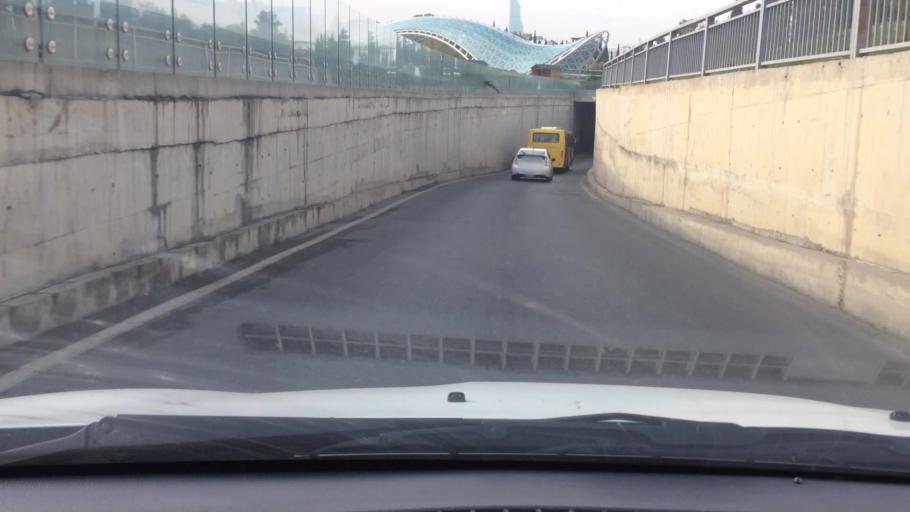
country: GE
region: T'bilisi
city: Tbilisi
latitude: 41.6916
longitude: 44.8104
